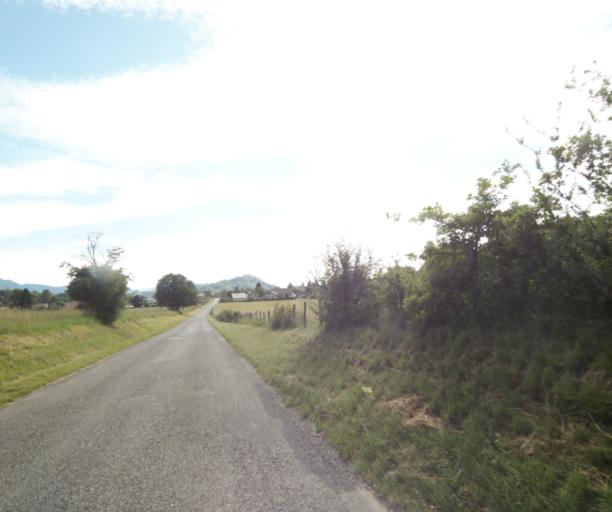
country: FR
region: Rhone-Alpes
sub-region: Departement de la Haute-Savoie
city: Thonon-les-Bains
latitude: 46.3487
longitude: 6.4913
